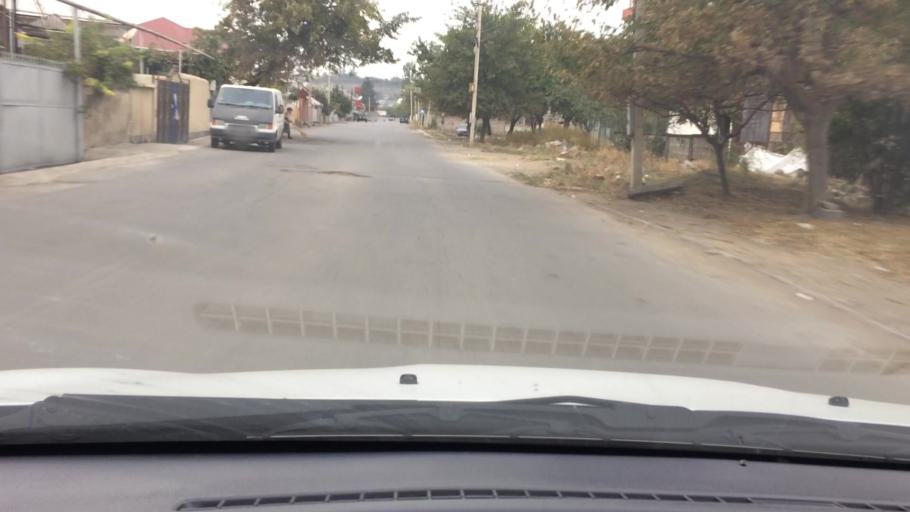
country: GE
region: Kvemo Kartli
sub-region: Marneuli
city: Marneuli
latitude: 41.4806
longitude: 44.7968
